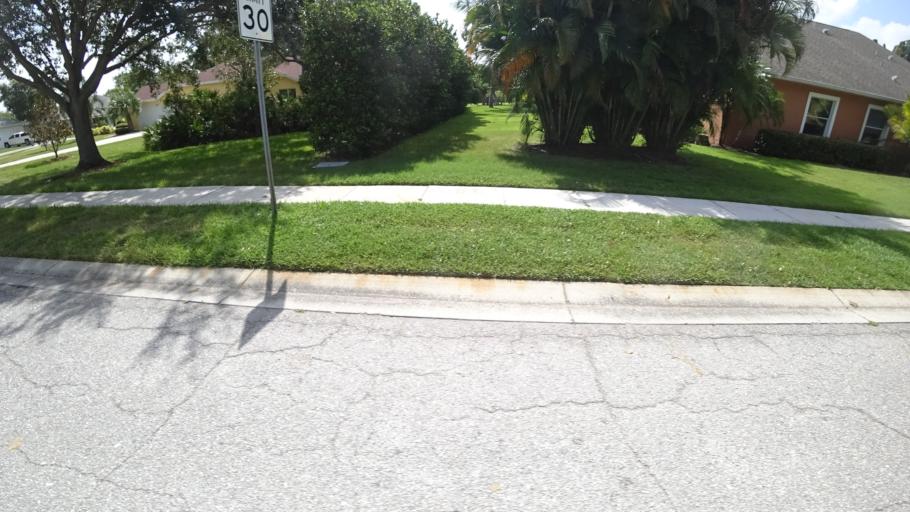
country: US
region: Florida
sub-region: Sarasota County
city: The Meadows
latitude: 27.4148
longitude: -82.4413
